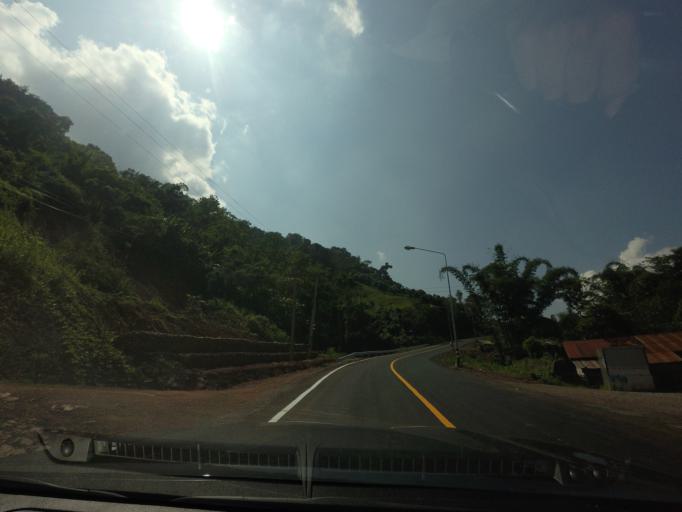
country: TH
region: Nan
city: Bo Kluea
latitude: 19.1736
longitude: 101.1709
